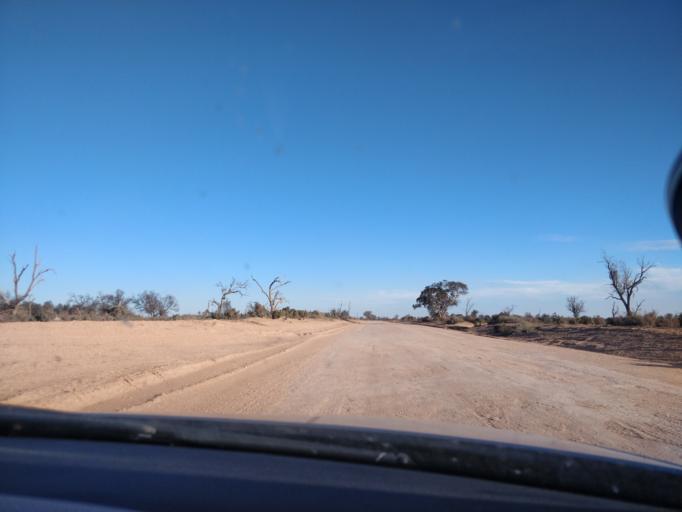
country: AU
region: New South Wales
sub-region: Wentworth
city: Gol Gol
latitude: -33.8672
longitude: 142.8869
